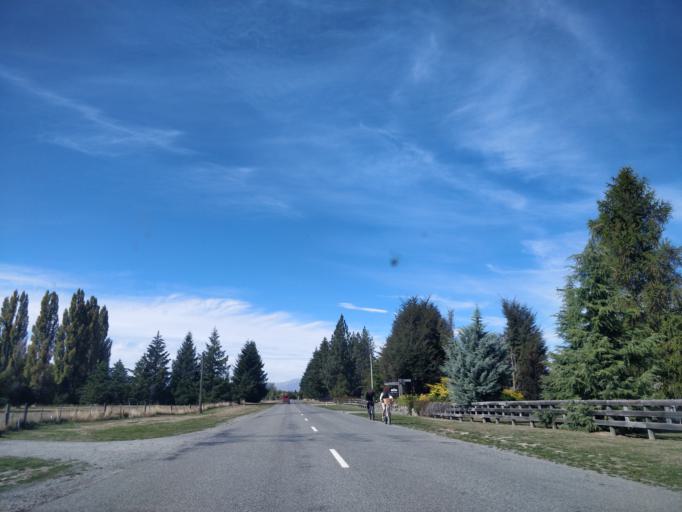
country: NZ
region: Canterbury
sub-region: Timaru District
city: Pleasant Point
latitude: -44.2438
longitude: 170.0898
